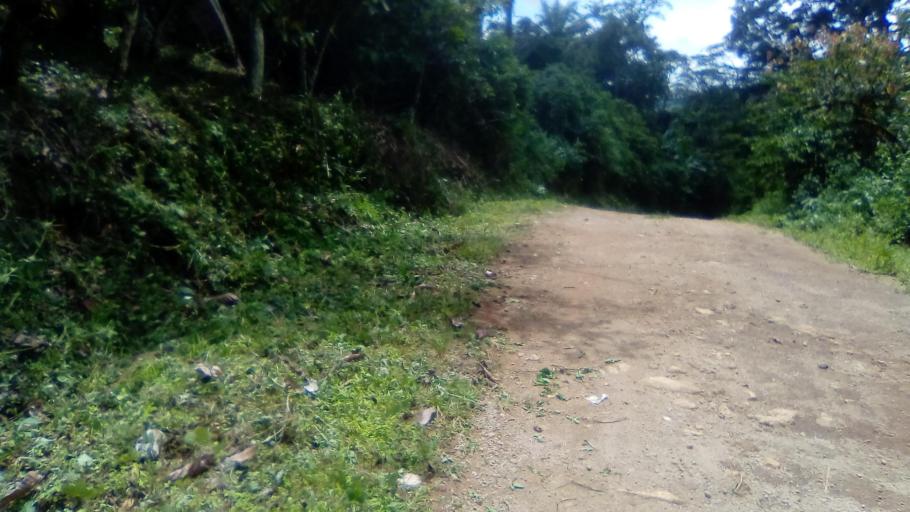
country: SL
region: Eastern Province
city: Giehun
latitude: 8.5033
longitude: -10.9055
